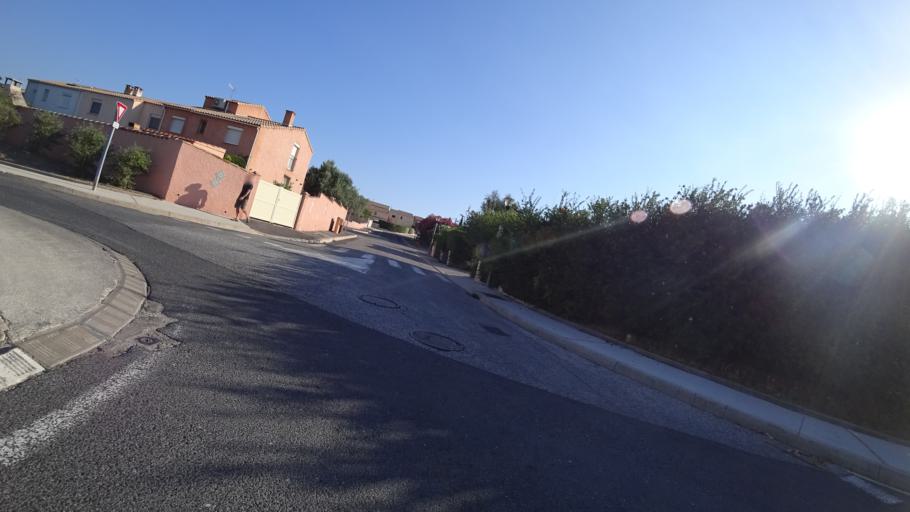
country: FR
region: Languedoc-Roussillon
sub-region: Departement des Pyrenees-Orientales
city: Canet-en-Roussillon
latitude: 42.6996
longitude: 3.0021
